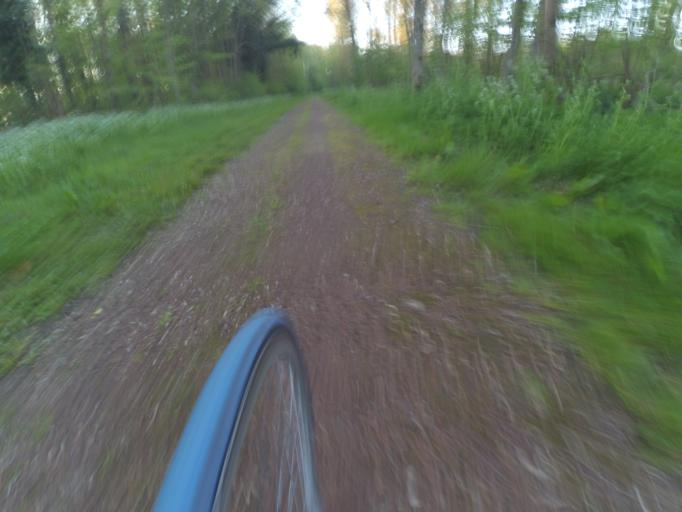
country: NL
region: Flevoland
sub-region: Gemeente Lelystad
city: Lelystad
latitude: 52.4313
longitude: 5.4976
